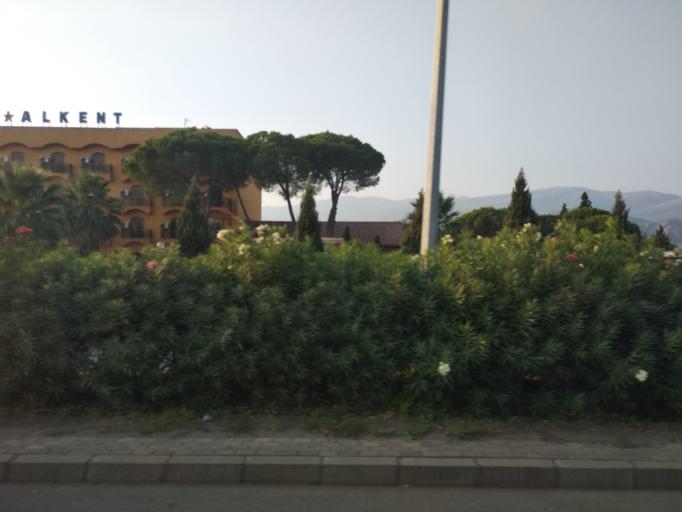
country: TR
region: Manisa
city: Salihli
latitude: 38.4947
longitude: 28.1800
